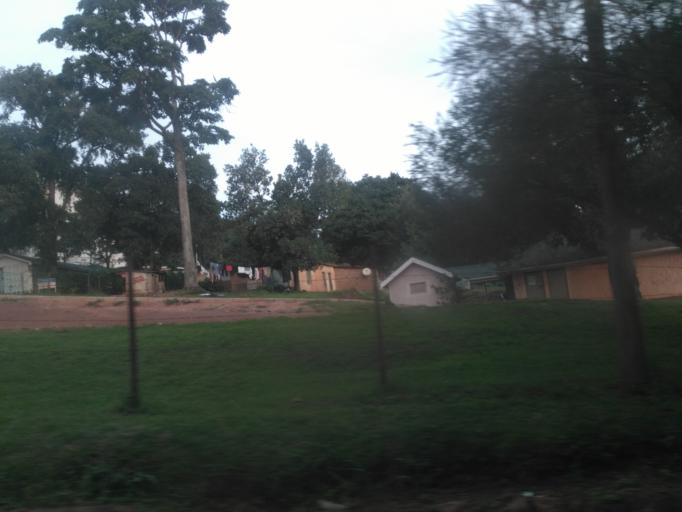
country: UG
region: Central Region
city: Kampala Central Division
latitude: 0.3396
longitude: 32.5772
